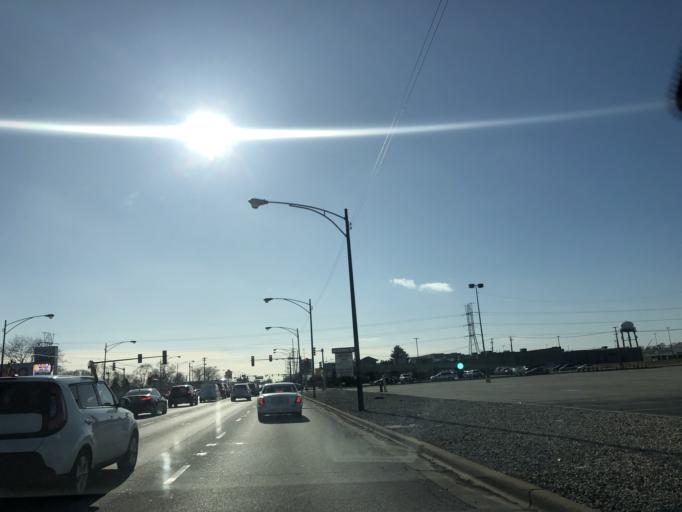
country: US
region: Illinois
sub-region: Cook County
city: Hometown
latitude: 41.7554
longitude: -87.7417
